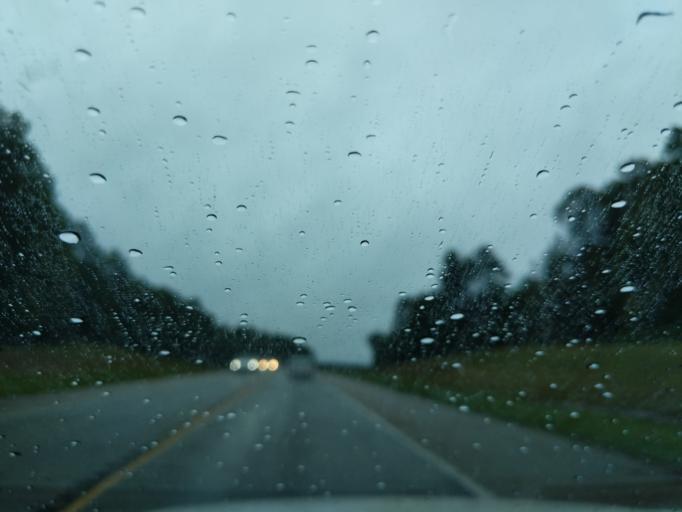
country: US
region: Louisiana
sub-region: Webster Parish
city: Minden
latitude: 32.5954
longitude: -93.2492
